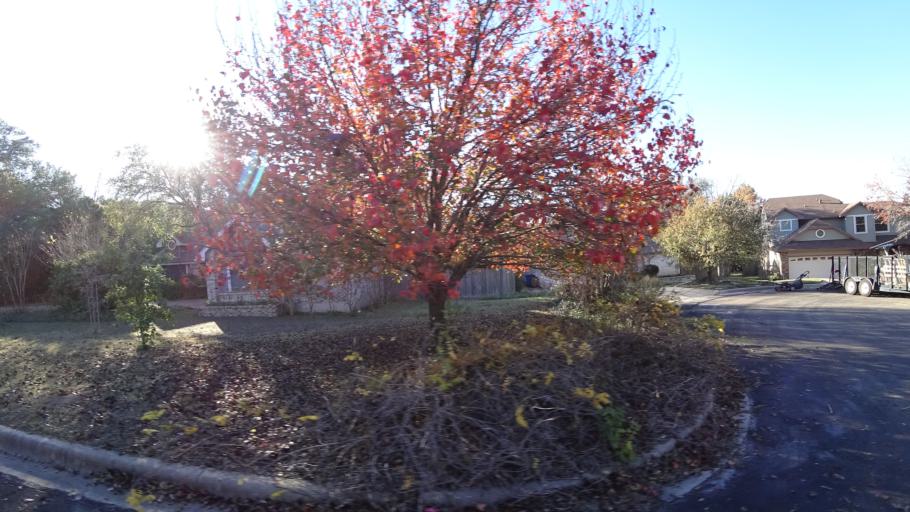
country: US
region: Texas
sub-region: Travis County
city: Wells Branch
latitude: 30.3981
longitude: -97.6989
